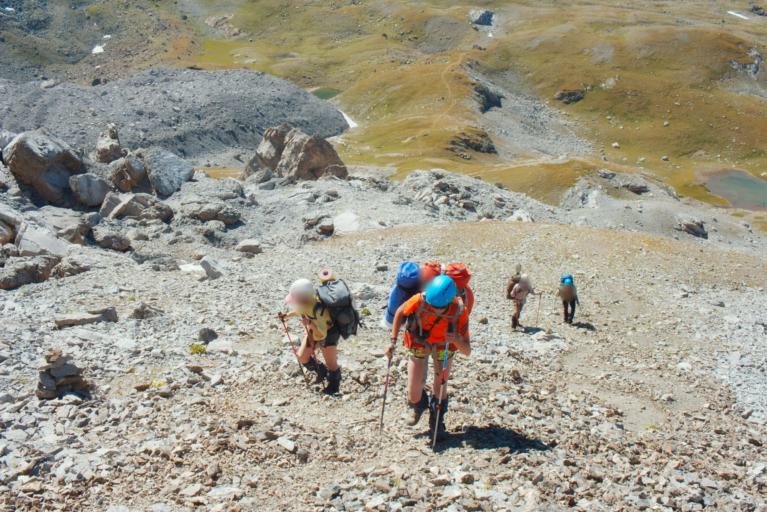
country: RU
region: Karachayevo-Cherkesiya
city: Nizhniy Arkhyz
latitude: 43.5943
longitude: 41.1853
